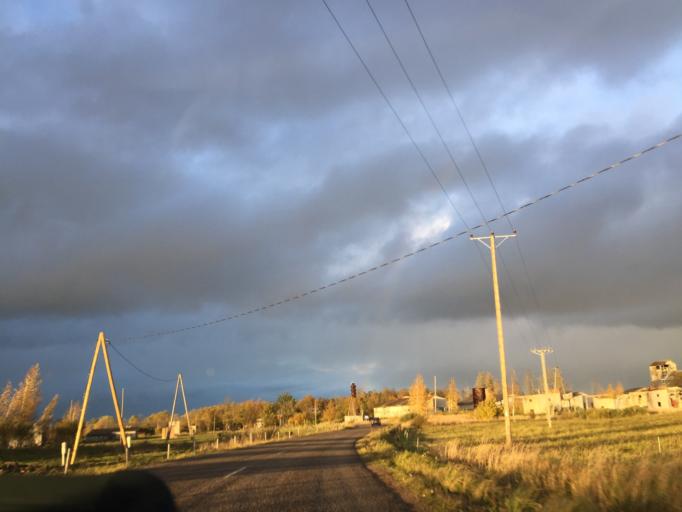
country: LV
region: Talsu Rajons
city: Sabile
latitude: 56.9447
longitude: 22.3983
